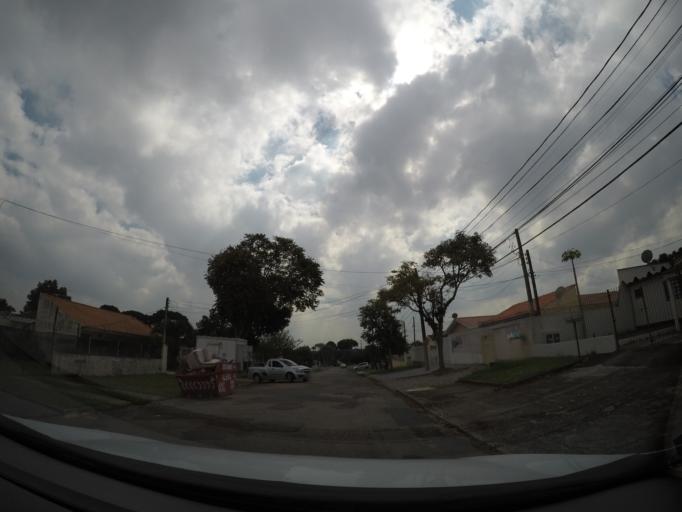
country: BR
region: Parana
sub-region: Sao Jose Dos Pinhais
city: Sao Jose dos Pinhais
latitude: -25.5037
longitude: -49.2461
